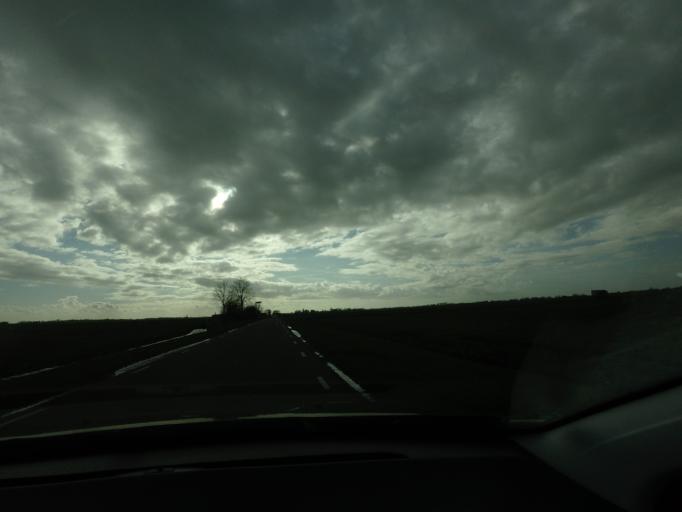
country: NL
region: Friesland
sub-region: Gemeente Boarnsterhim
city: Jirnsum
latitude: 53.0744
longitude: 5.7741
